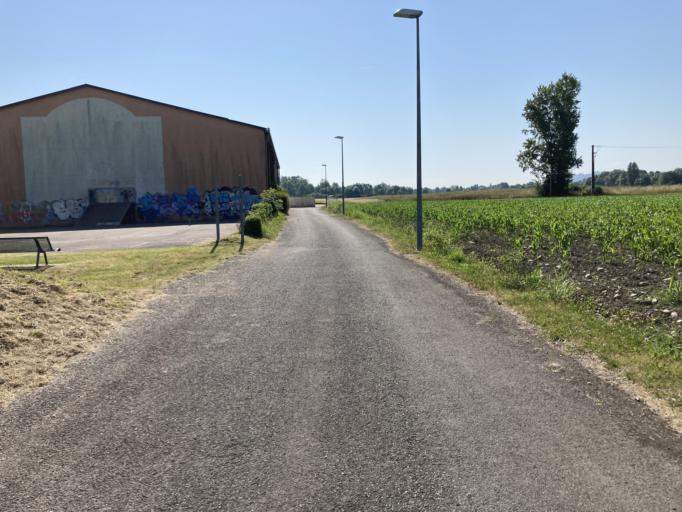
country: FR
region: Aquitaine
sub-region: Departement des Pyrenees-Atlantiques
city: Artiguelouve
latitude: 43.3268
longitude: -0.4769
